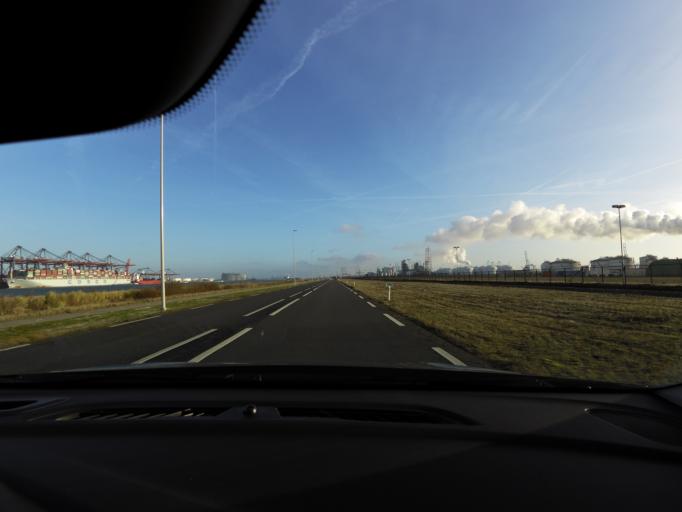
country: NL
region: South Holland
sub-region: Gemeente Rotterdam
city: Hoek van Holland
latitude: 51.9713
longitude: 4.0229
